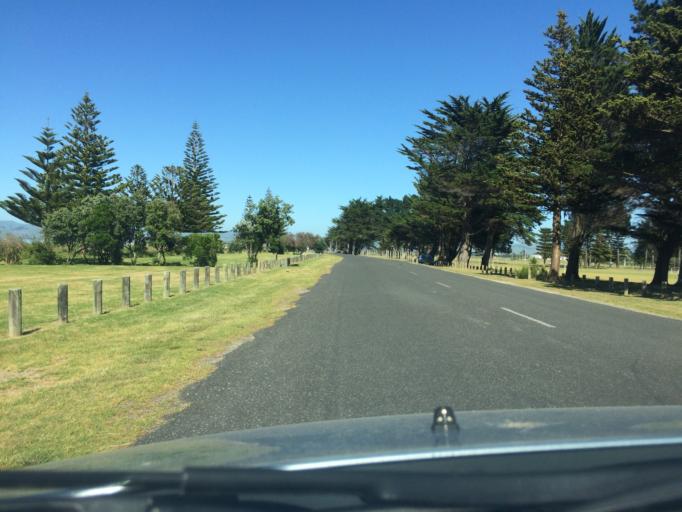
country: NZ
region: Gisborne
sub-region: Gisborne District
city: Gisborne
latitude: -38.6725
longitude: 177.9955
